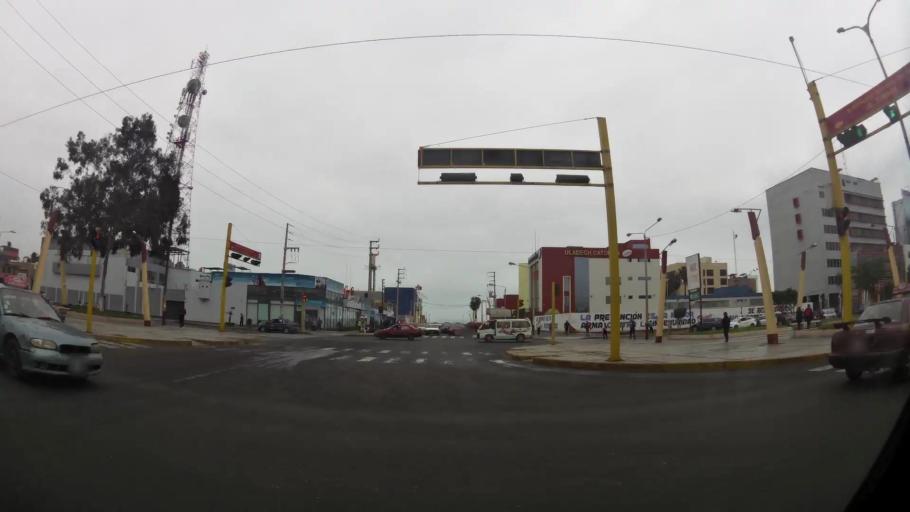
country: PE
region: Ancash
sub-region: Provincia de Santa
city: Chimbote
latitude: -9.0765
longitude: -78.5889
